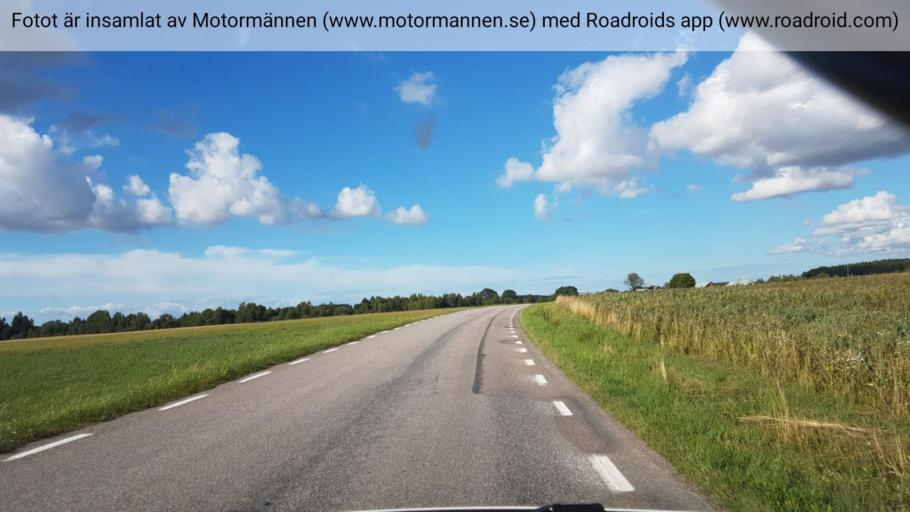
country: SE
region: Vaestra Goetaland
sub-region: Lidkopings Kommun
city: Vinninga
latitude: 58.4394
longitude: 13.3378
